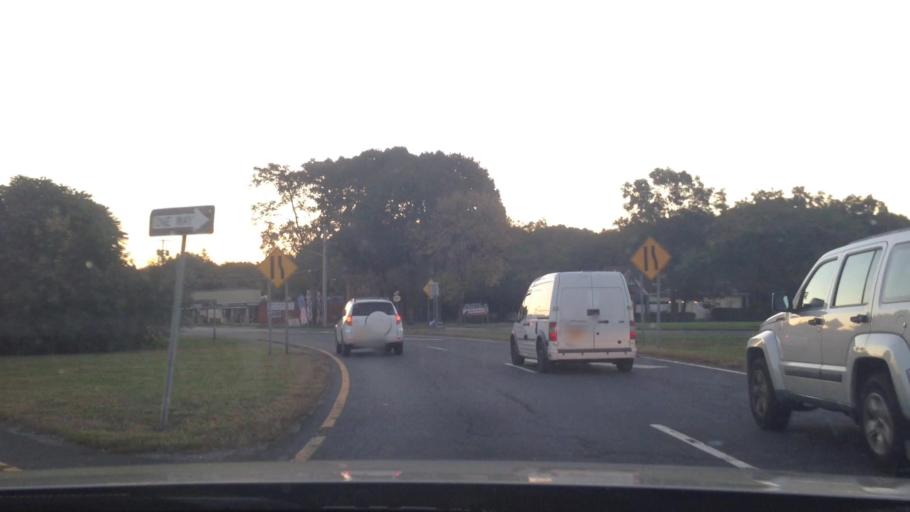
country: US
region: New York
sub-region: Suffolk County
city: Mount Sinai
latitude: 40.9325
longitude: -73.0325
